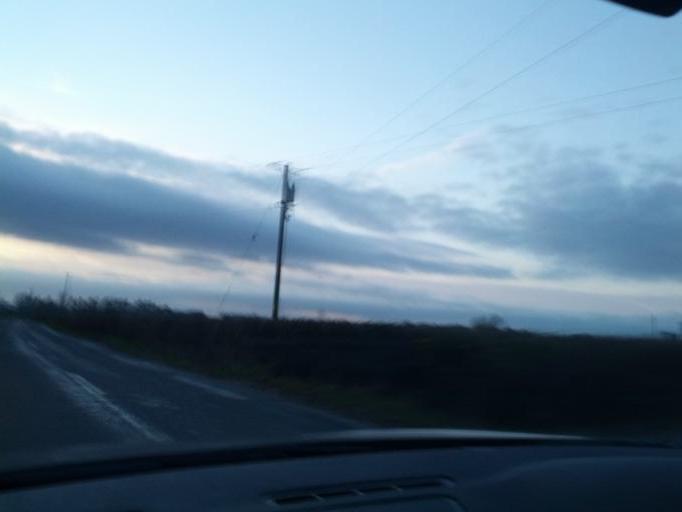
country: IE
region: Leinster
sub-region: Uibh Fhaili
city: Banagher
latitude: 53.1085
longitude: -8.0718
